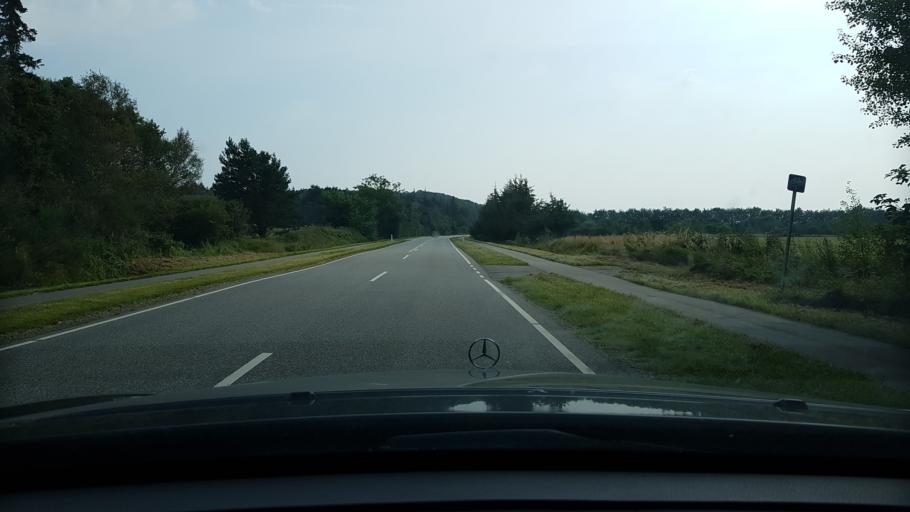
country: DK
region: North Denmark
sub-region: Alborg Kommune
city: Hals
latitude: 56.9231
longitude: 10.2614
